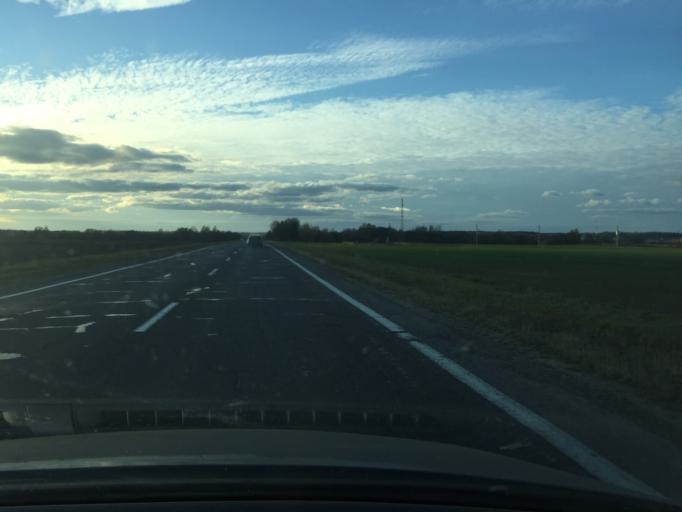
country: BY
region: Vitebsk
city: Vyerkhnyadzvinsk
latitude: 55.8368
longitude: 27.9008
